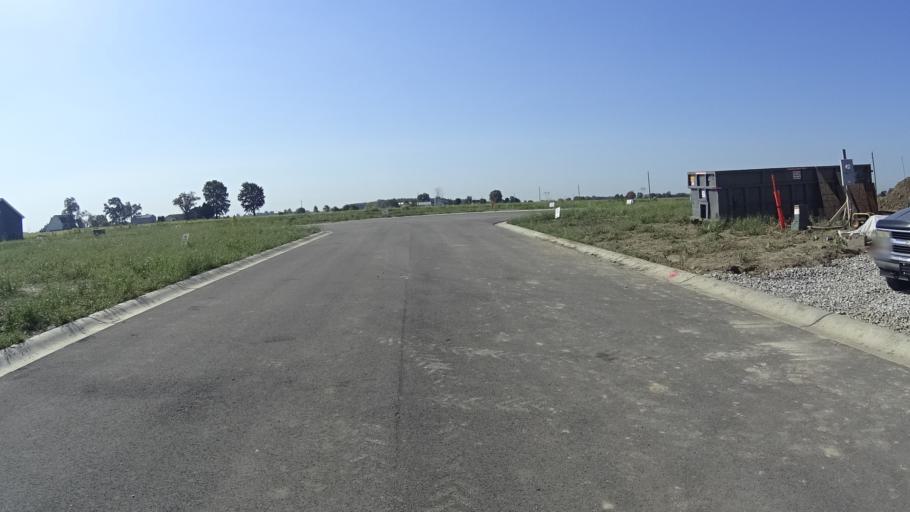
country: US
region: Indiana
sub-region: Madison County
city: Lapel
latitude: 40.0573
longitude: -85.8527
